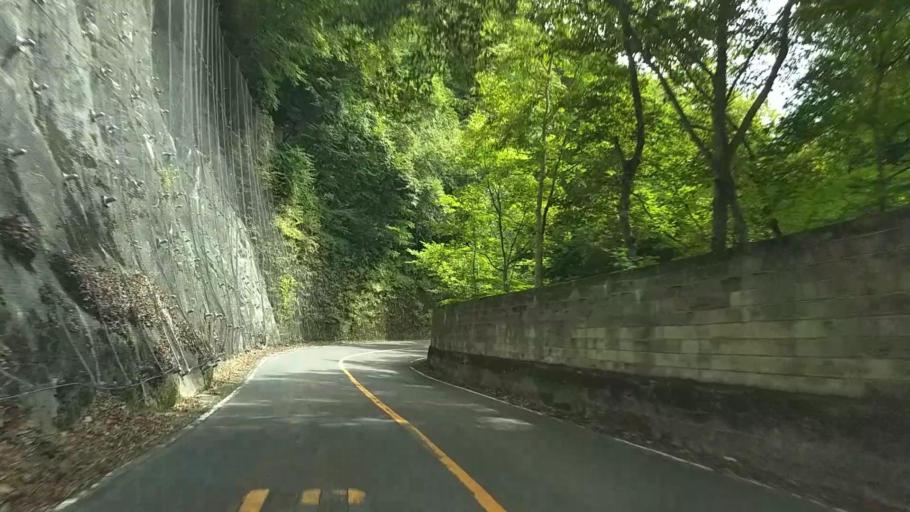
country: JP
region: Tochigi
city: Nikko
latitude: 36.7273
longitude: 139.4860
